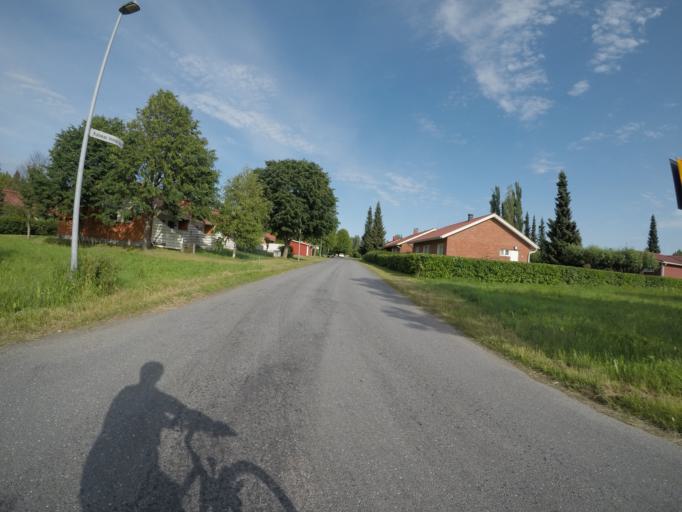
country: FI
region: Haeme
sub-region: Haemeenlinna
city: Haemeenlinna
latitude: 60.9798
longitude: 24.4276
